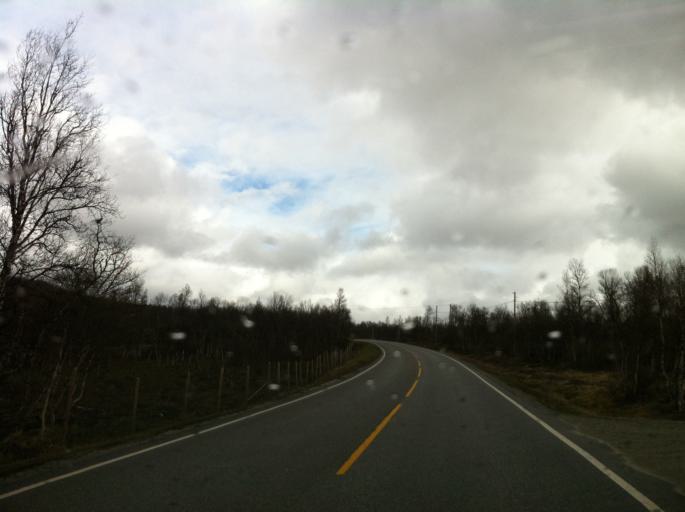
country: NO
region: Sor-Trondelag
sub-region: Tydal
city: Aas
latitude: 62.6394
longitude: 11.8947
